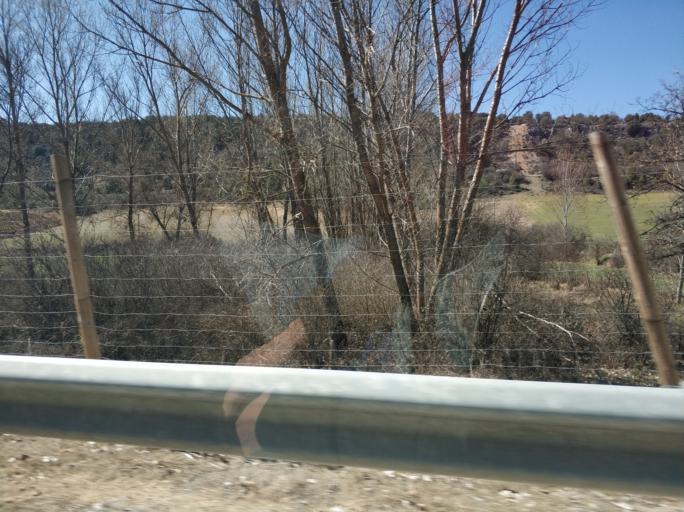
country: ES
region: Castille and Leon
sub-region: Provincia de Soria
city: Casarejos
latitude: 41.8015
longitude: -3.0419
